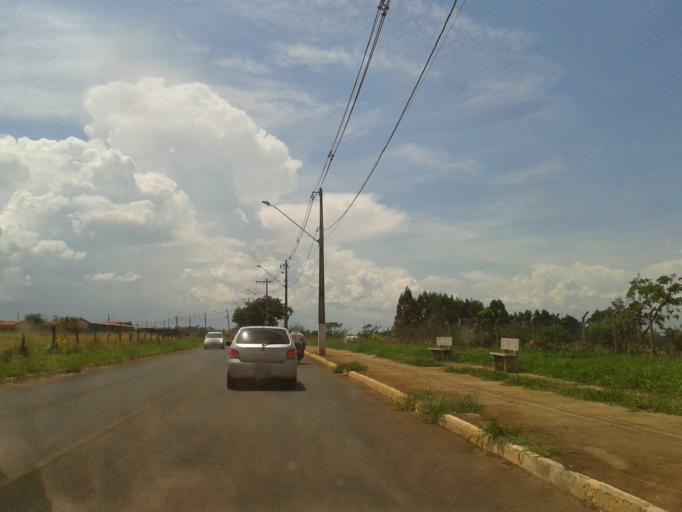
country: BR
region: Minas Gerais
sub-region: Araguari
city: Araguari
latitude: -18.6754
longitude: -48.1950
